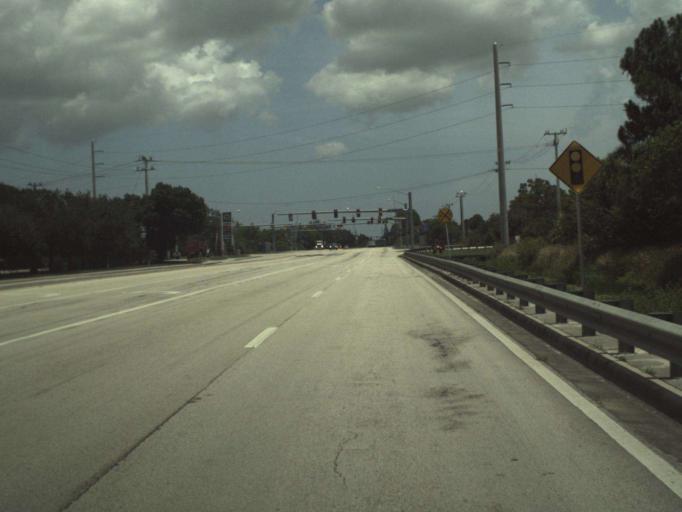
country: US
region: Florida
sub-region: Saint Lucie County
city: Fort Pierce South
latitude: 27.3744
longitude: -80.3945
